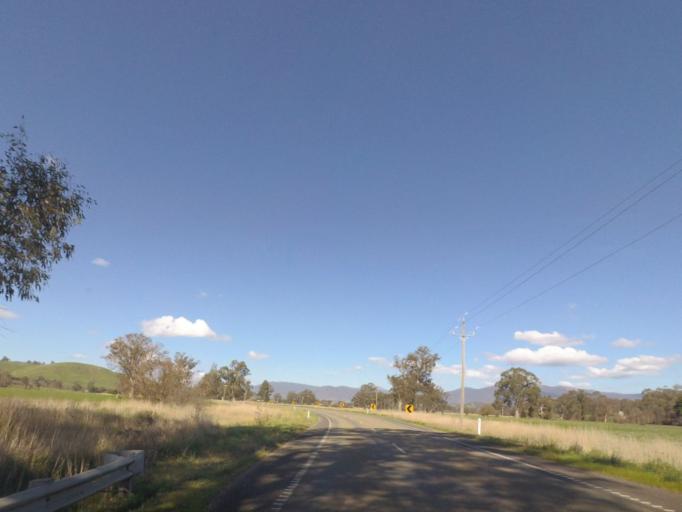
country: AU
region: Victoria
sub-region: Murrindindi
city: Alexandra
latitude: -37.2257
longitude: 145.7431
